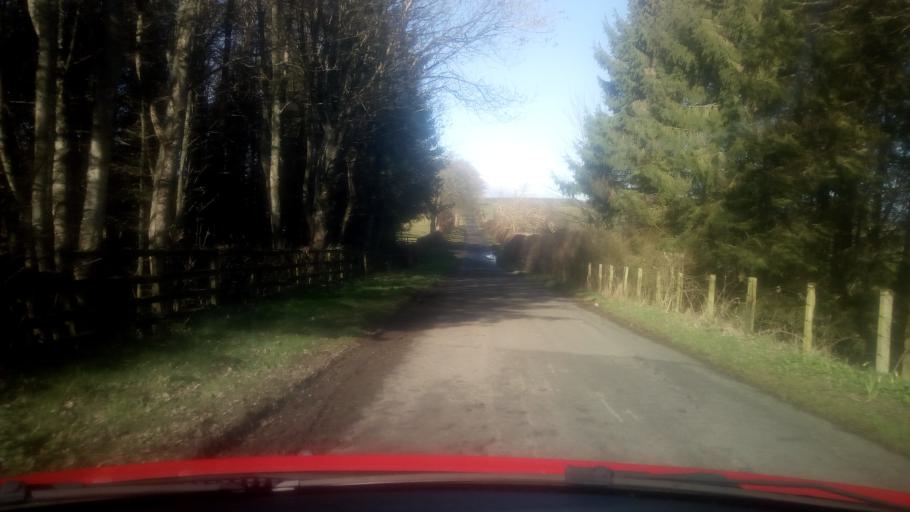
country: GB
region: Scotland
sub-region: The Scottish Borders
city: Saint Boswells
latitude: 55.5360
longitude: -2.6538
